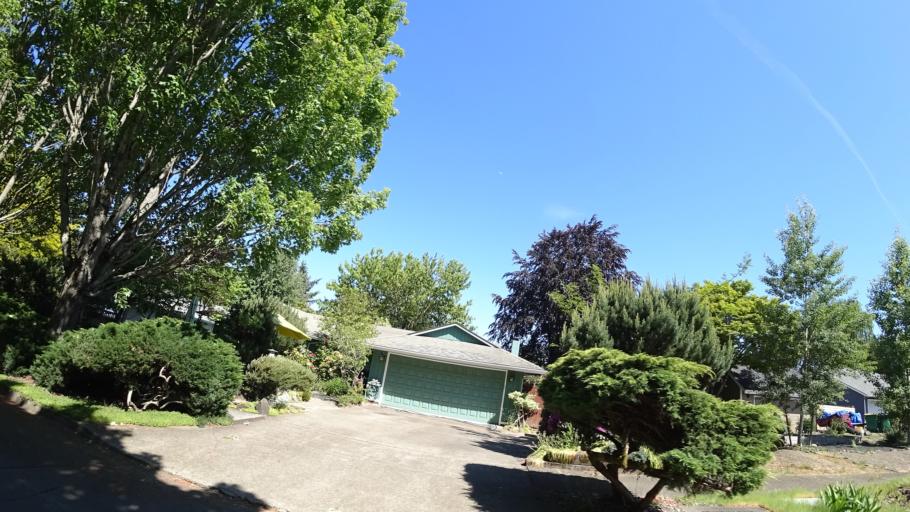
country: US
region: Oregon
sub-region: Washington County
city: Beaverton
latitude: 45.4528
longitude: -122.7991
